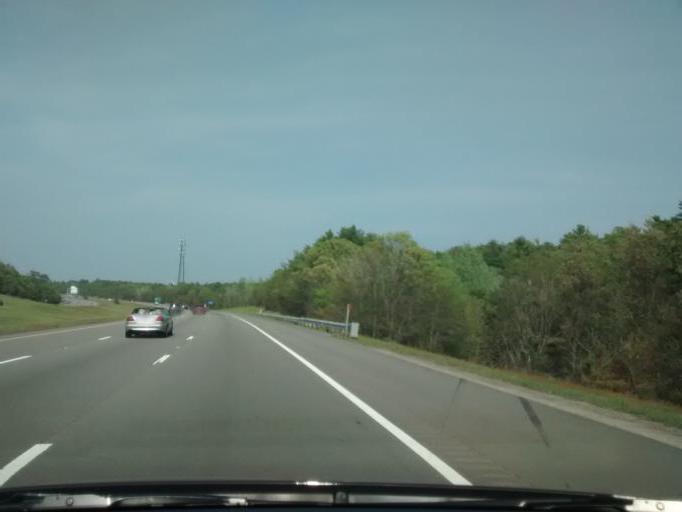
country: US
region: Massachusetts
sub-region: Plymouth County
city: Onset
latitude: 41.7642
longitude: -70.6597
